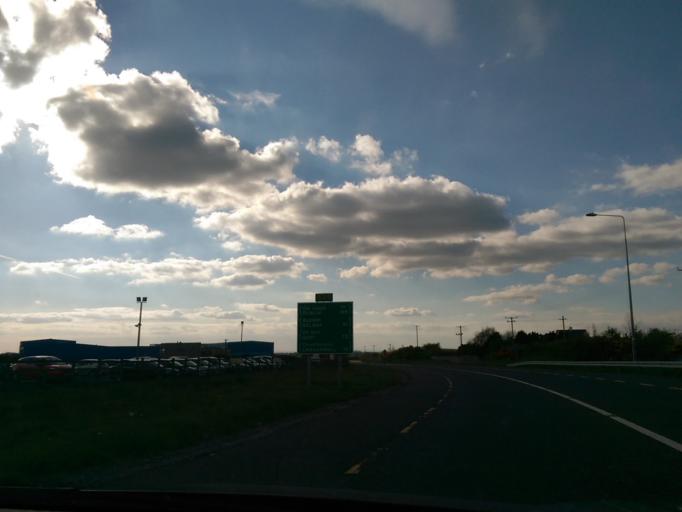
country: IE
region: Connaught
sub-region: County Galway
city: Loughrea
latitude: 53.2045
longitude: -8.5430
